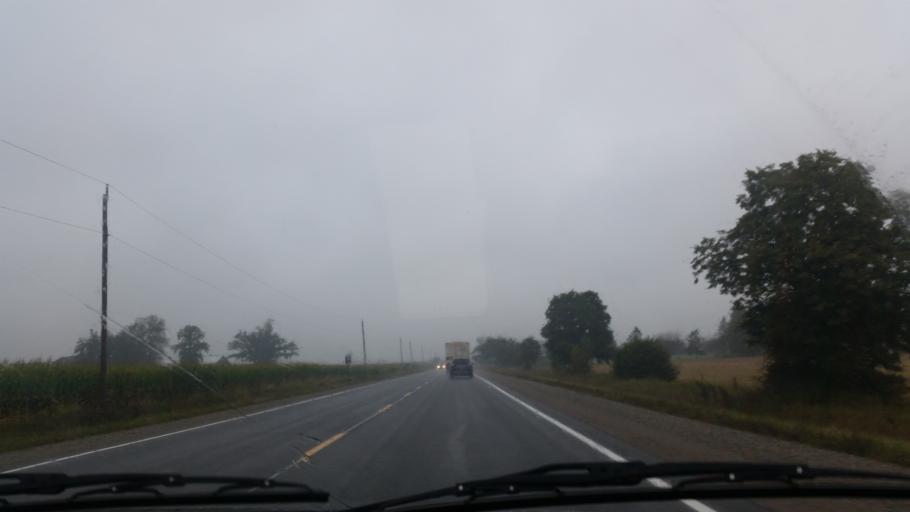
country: CA
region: Ontario
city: London
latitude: 43.2130
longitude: -81.1922
